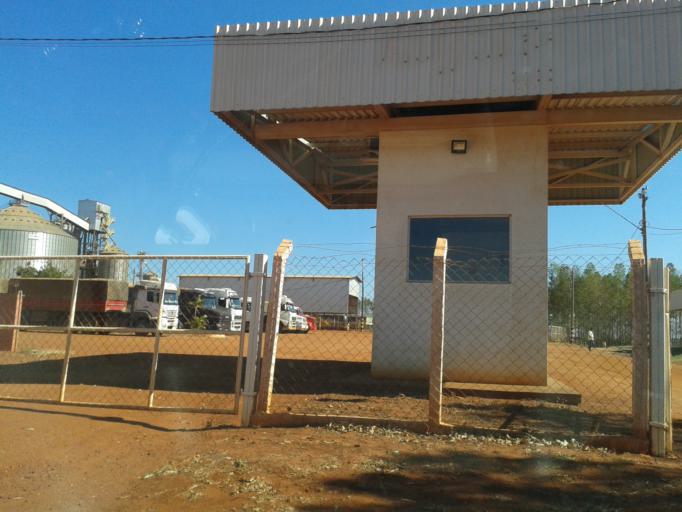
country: BR
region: Minas Gerais
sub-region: Capinopolis
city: Capinopolis
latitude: -18.7394
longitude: -49.5499
